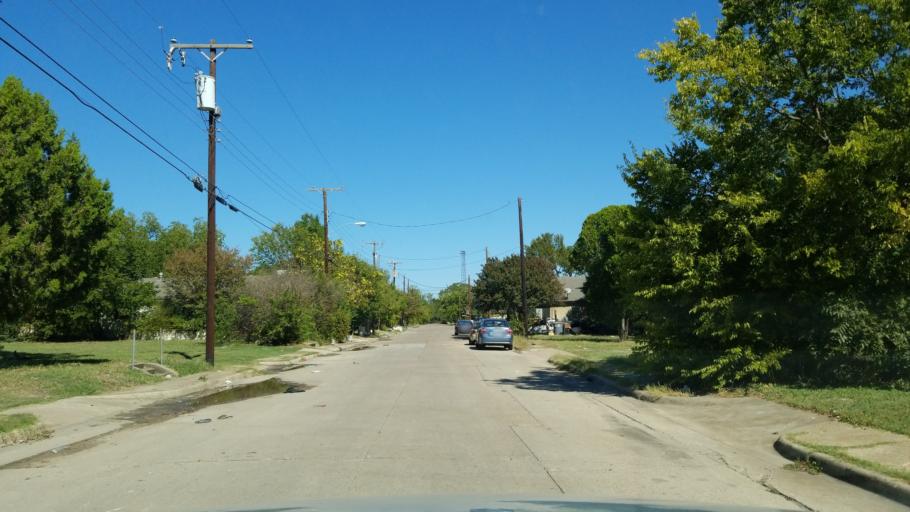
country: US
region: Texas
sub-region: Dallas County
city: Dallas
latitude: 32.7774
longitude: -96.7470
